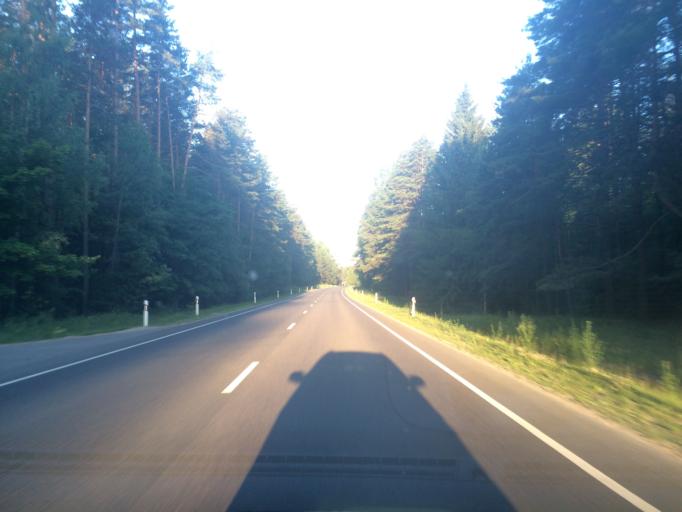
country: LT
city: Zarasai
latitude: 55.7062
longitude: 26.1792
